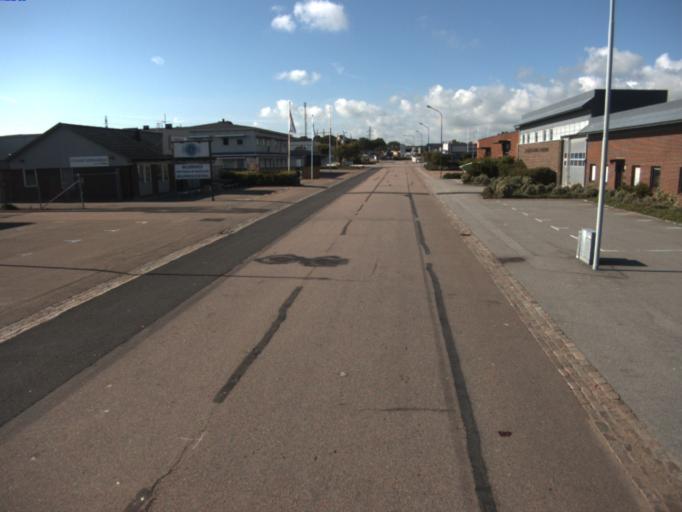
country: SE
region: Skane
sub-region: Helsingborg
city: Odakra
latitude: 56.0758
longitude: 12.7197
